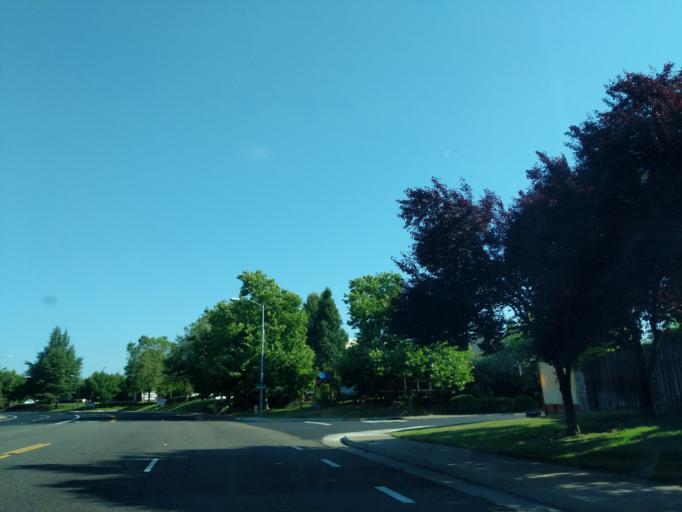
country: US
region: California
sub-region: Sacramento County
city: Folsom
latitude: 38.6674
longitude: -121.1595
